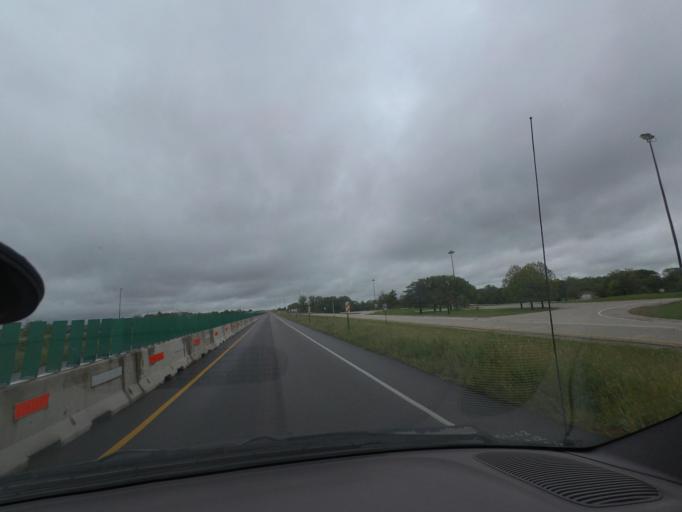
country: US
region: Illinois
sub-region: Piatt County
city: Cerro Gordo
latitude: 39.9911
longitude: -88.7846
